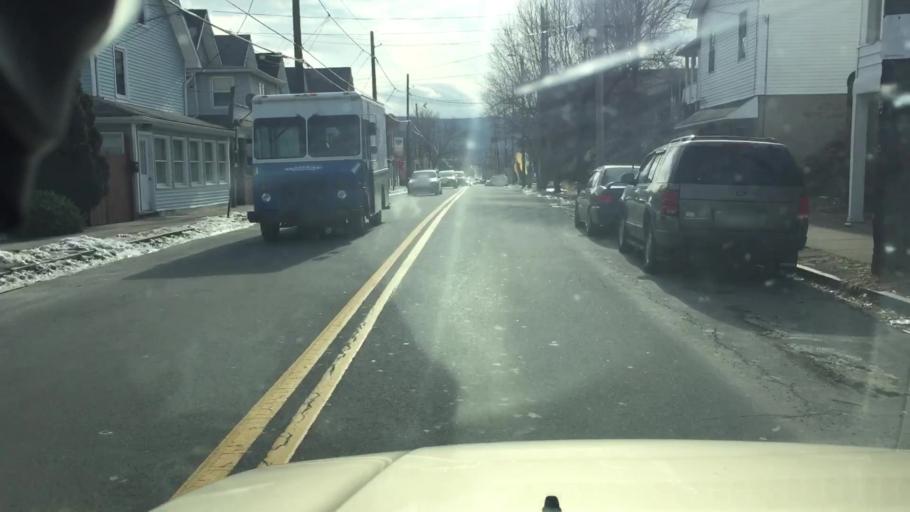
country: US
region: Pennsylvania
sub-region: Luzerne County
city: Wilkes-Barre
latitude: 41.2303
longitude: -75.8912
